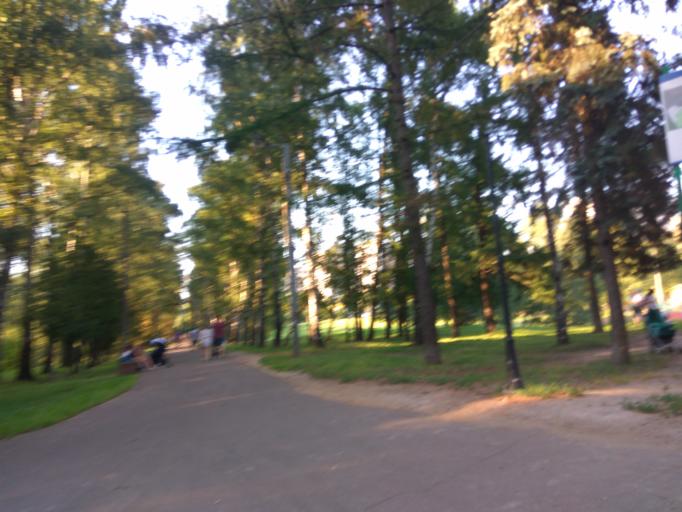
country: RU
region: Moskovskaya
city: Levoberezhnyy
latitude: 55.8537
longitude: 37.4803
